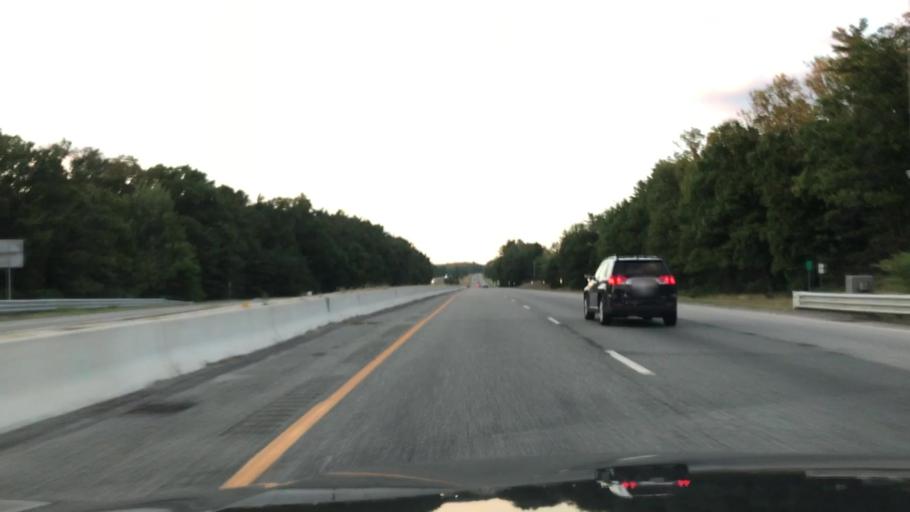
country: US
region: Rhode Island
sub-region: Washington County
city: Hope Valley
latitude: 41.5380
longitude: -71.6787
